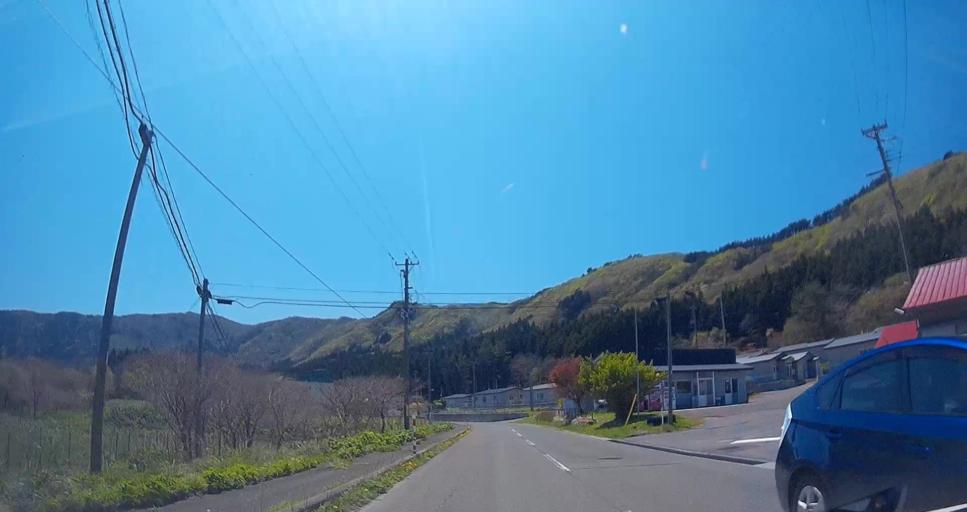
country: JP
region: Aomori
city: Mutsu
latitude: 41.4084
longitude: 141.4478
